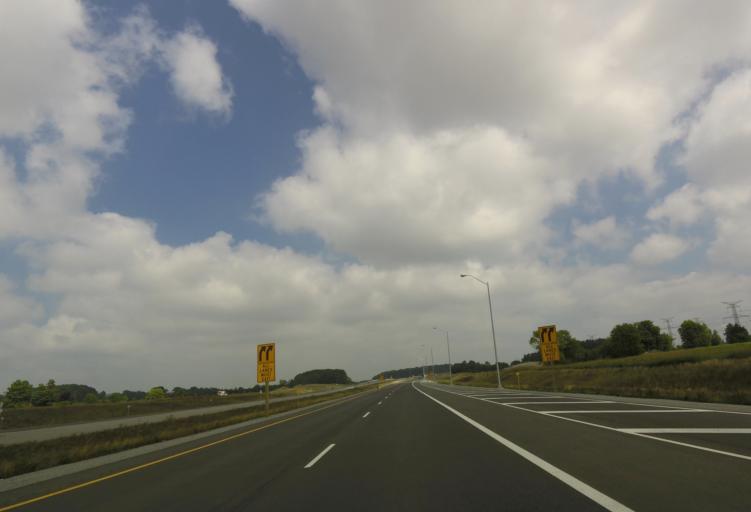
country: CA
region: Ontario
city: Oshawa
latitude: 43.9791
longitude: -78.8809
